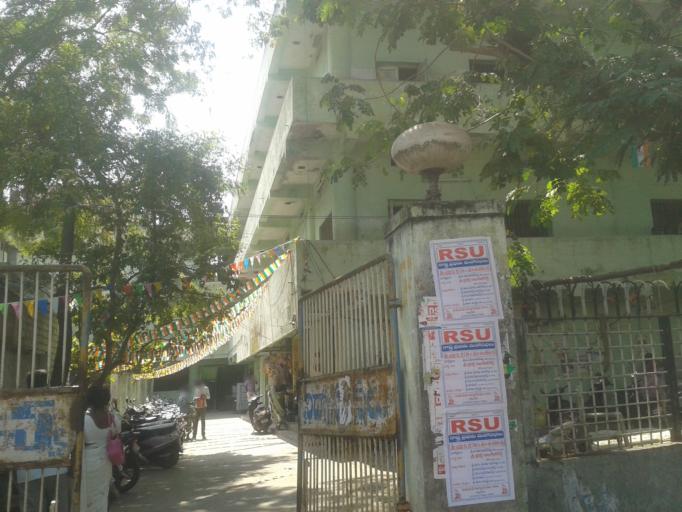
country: IN
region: Andhra Pradesh
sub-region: Chittoor
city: Tirupati
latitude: 13.6312
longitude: 79.4187
